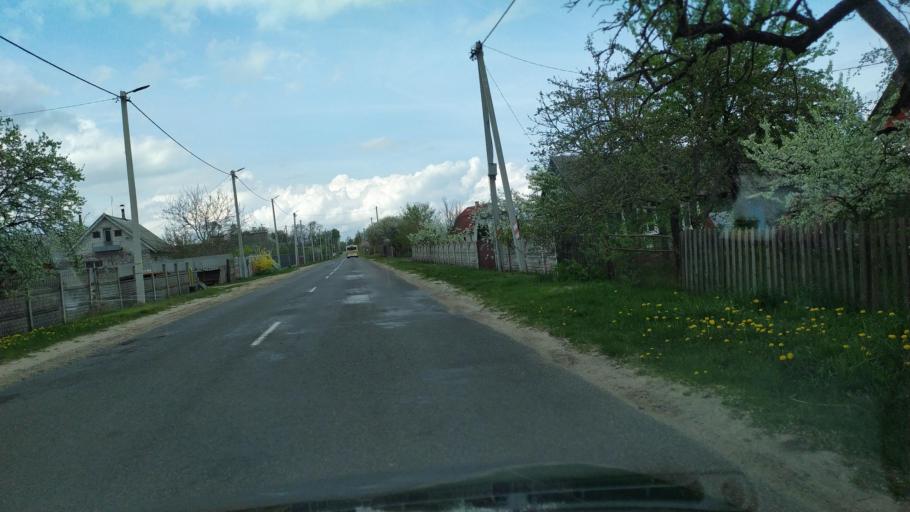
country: BY
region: Brest
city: Pruzhany
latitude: 52.5796
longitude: 24.4123
